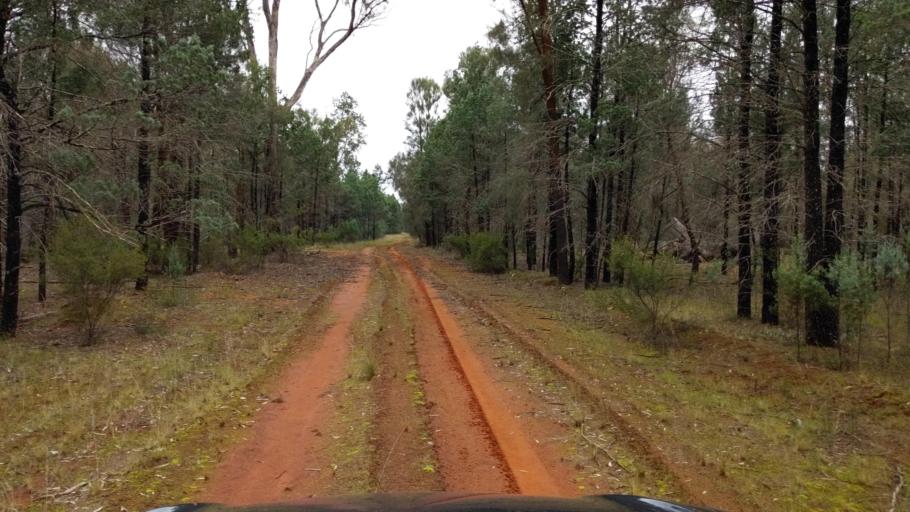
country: AU
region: New South Wales
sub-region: Coolamon
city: Coolamon
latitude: -34.8485
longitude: 146.9323
